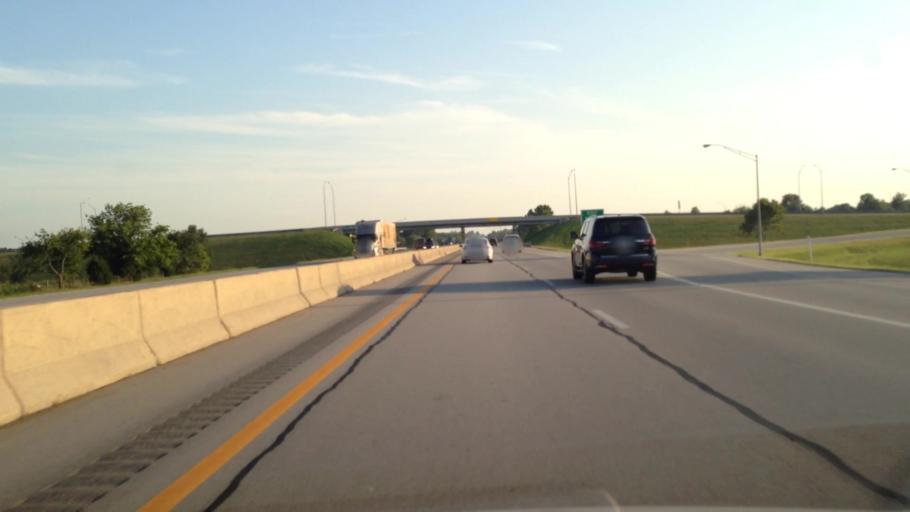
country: US
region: Oklahoma
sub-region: Ottawa County
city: Miami
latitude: 36.8676
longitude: -94.8490
